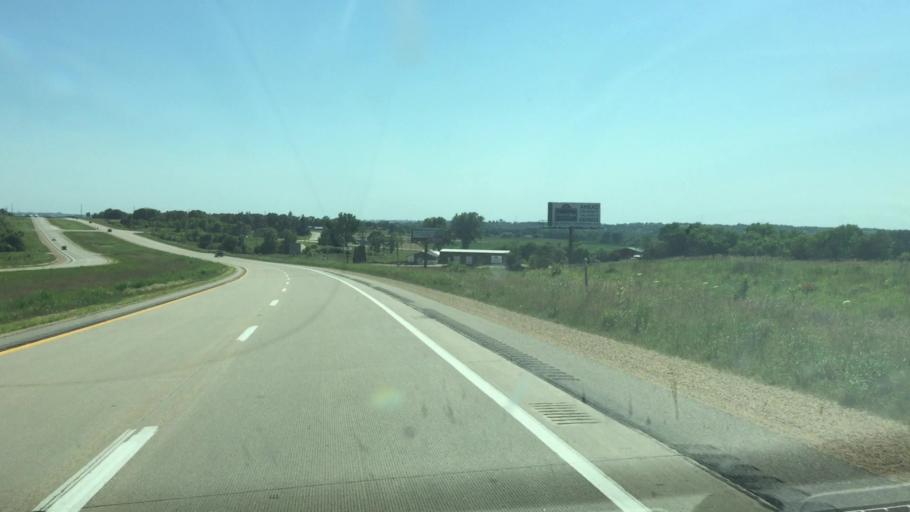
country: US
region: Iowa
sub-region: Jones County
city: Monticello
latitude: 42.2610
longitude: -91.1524
